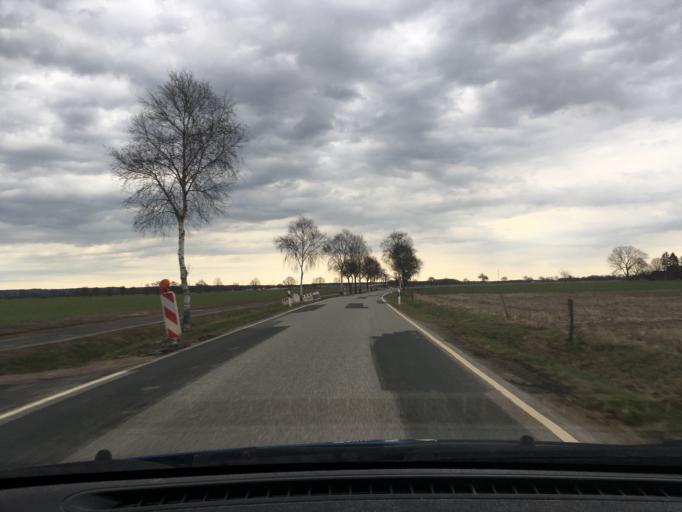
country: DE
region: Lower Saxony
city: Handorf
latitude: 53.3763
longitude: 10.3155
